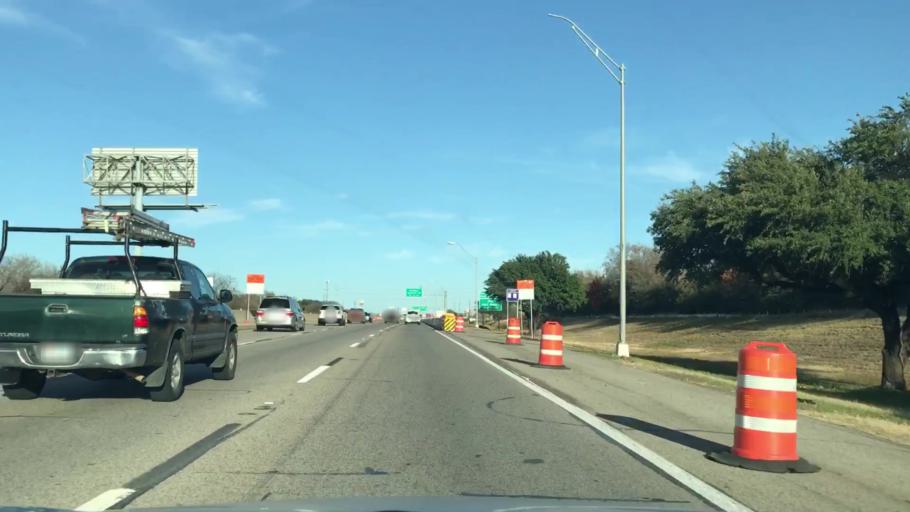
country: US
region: Texas
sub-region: Tarrant County
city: Richland Hills
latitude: 32.7971
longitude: -97.2305
